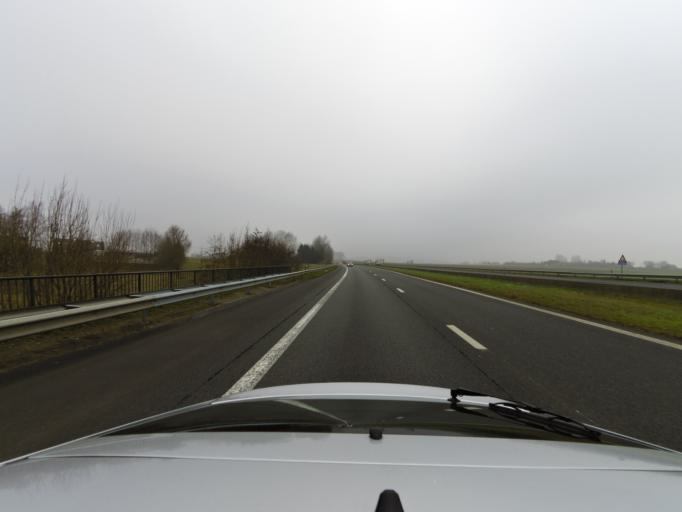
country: BE
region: Wallonia
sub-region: Province du Hainaut
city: Estaimpuis
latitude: 50.7469
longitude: 3.2938
